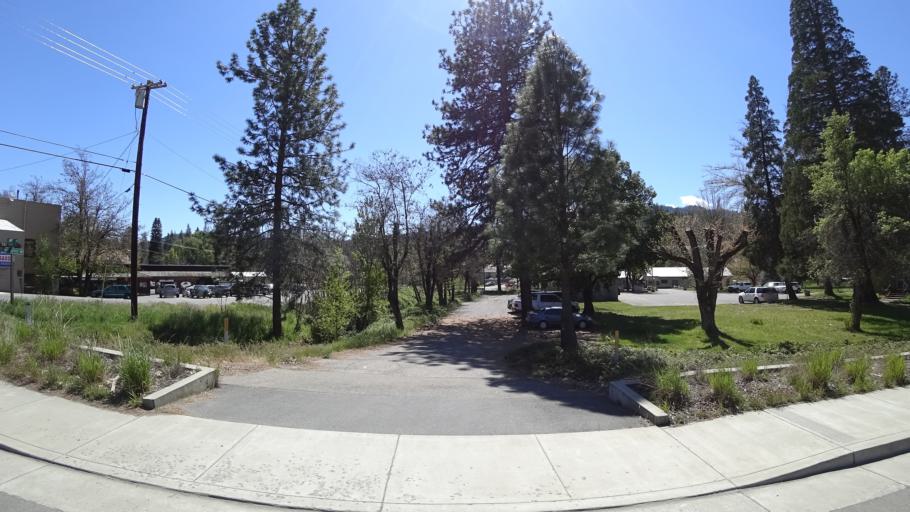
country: US
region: California
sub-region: Trinity County
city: Weaverville
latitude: 40.7347
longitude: -122.9419
